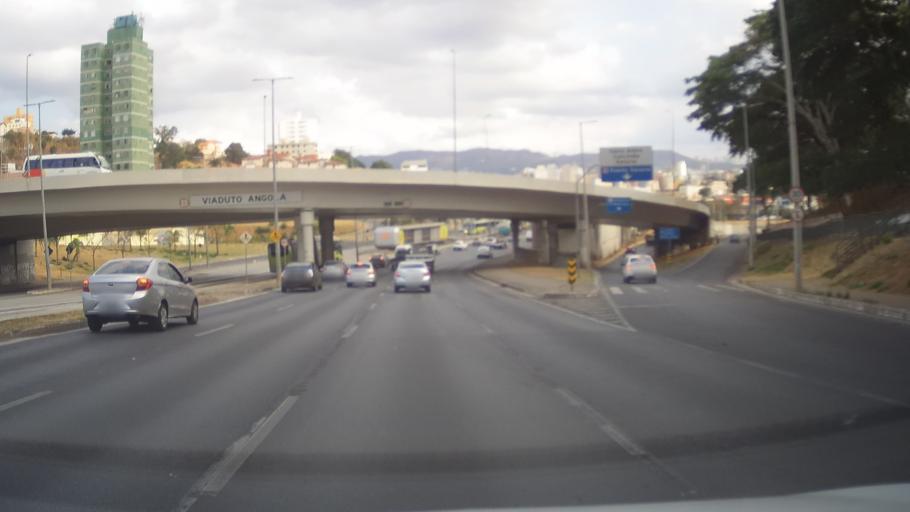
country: BR
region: Minas Gerais
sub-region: Belo Horizonte
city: Belo Horizonte
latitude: -19.9017
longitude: -43.9456
